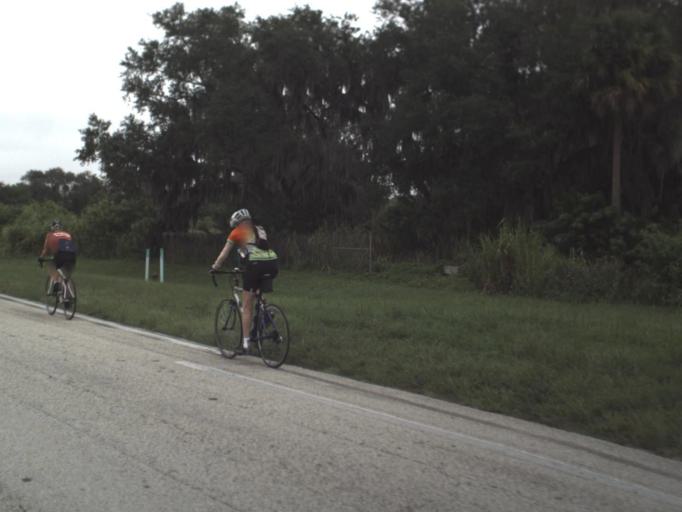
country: US
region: Florida
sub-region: Manatee County
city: Memphis
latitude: 27.6072
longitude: -82.5395
